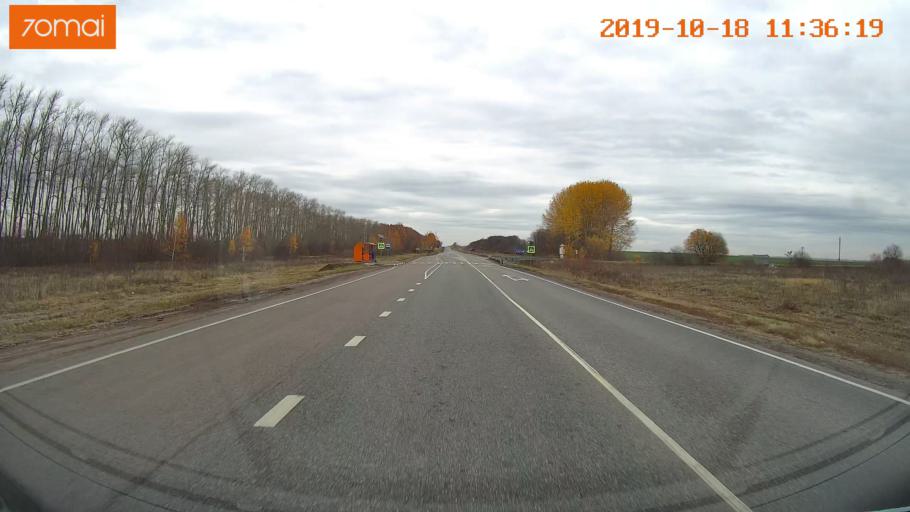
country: RU
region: Rjazan
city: Oktyabr'skiy
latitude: 54.1396
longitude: 38.8040
